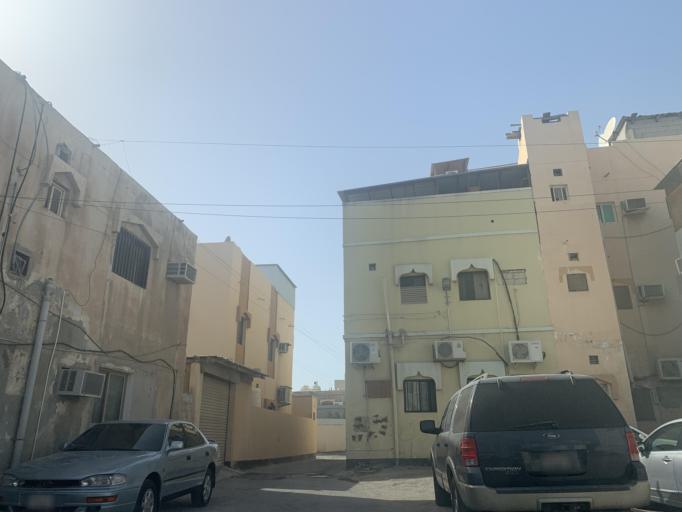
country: BH
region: Northern
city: Sitrah
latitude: 26.1623
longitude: 50.6184
